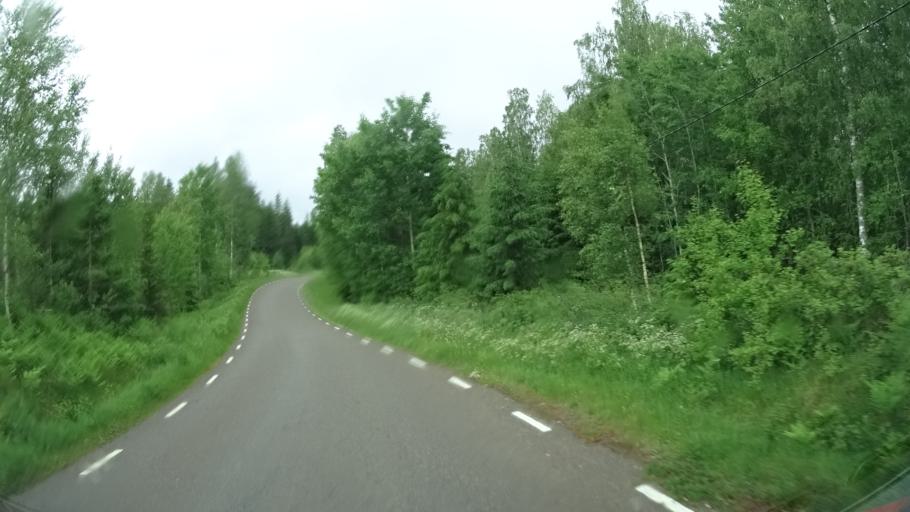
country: SE
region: Kalmar
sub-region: Vimmerby Kommun
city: Sodra Vi
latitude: 57.7092
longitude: 15.7638
